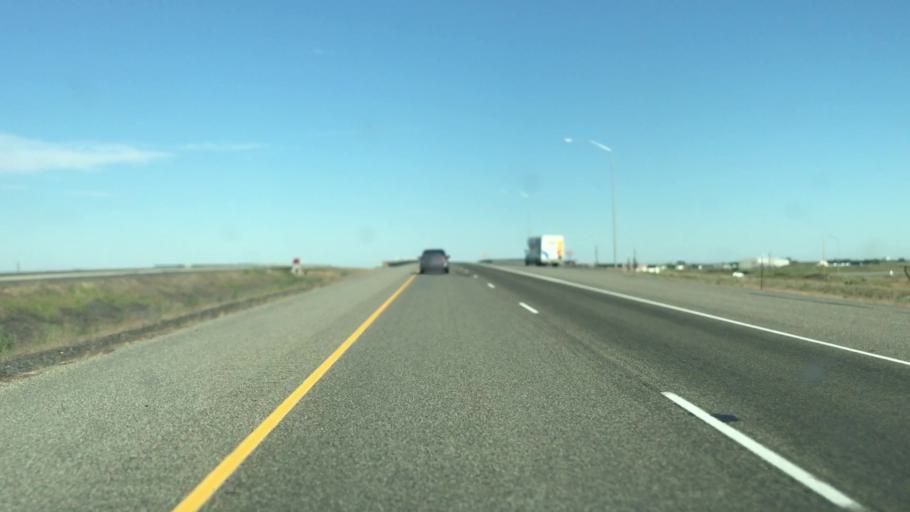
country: US
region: Idaho
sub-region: Twin Falls County
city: Twin Falls
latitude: 42.6412
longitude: -114.4424
